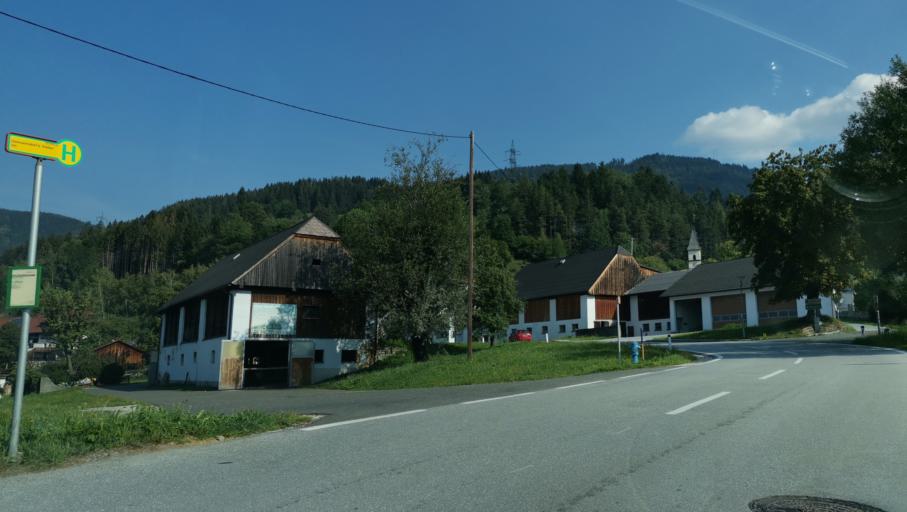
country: AT
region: Styria
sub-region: Politischer Bezirk Liezen
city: Trieben
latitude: 47.5031
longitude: 14.4767
